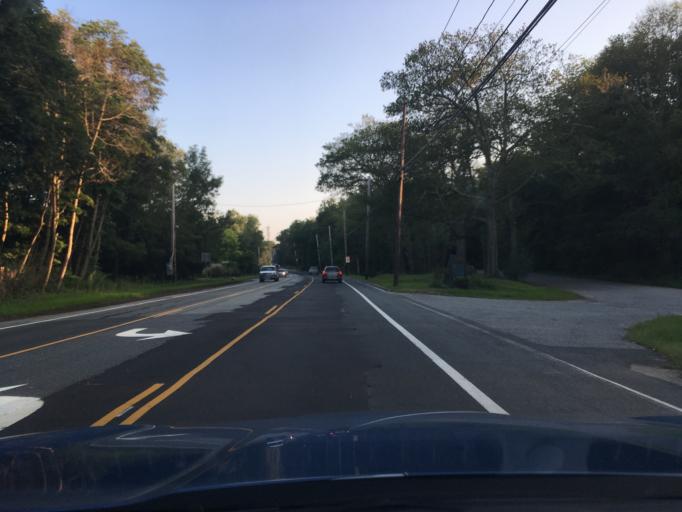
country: US
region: Rhode Island
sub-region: Washington County
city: North Kingstown
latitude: 41.5830
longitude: -71.4595
